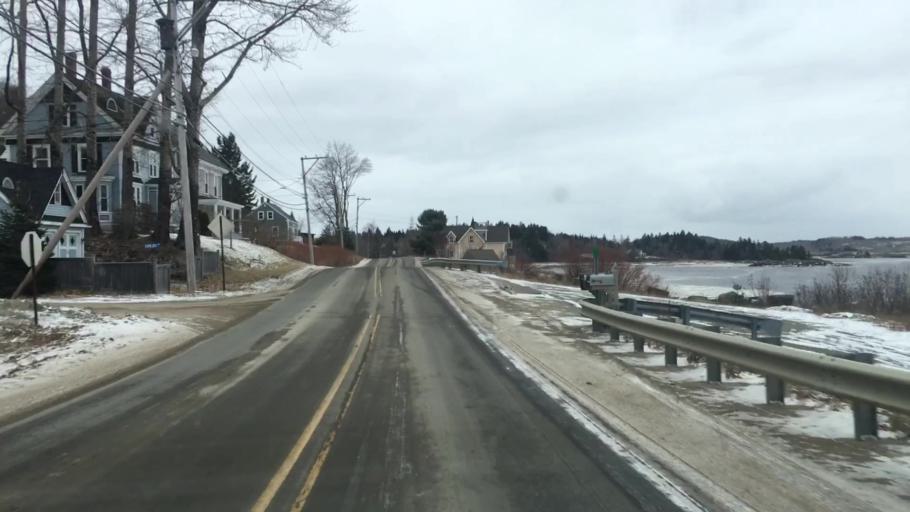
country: US
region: Maine
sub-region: Washington County
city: Machiasport
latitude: 44.6988
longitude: -67.3942
